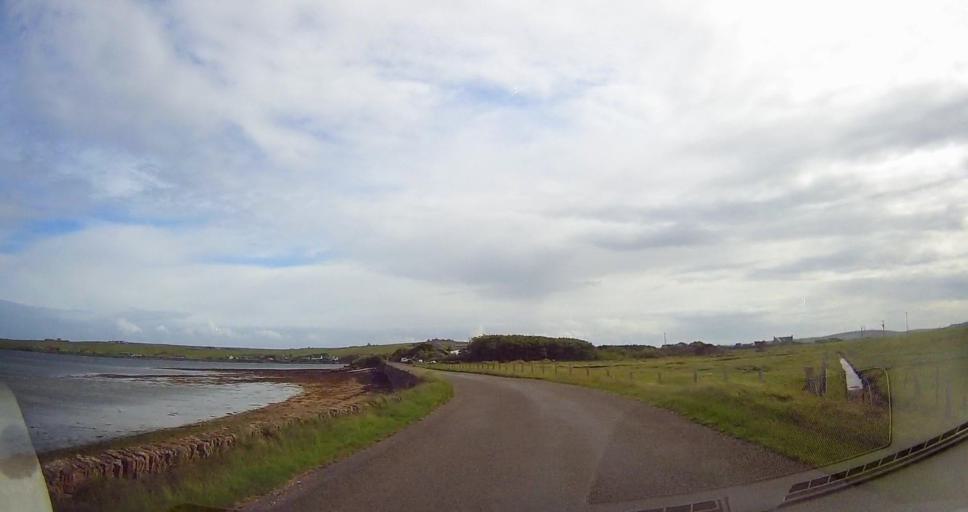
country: GB
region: Scotland
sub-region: Orkney Islands
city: Stromness
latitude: 58.8087
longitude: -3.2037
